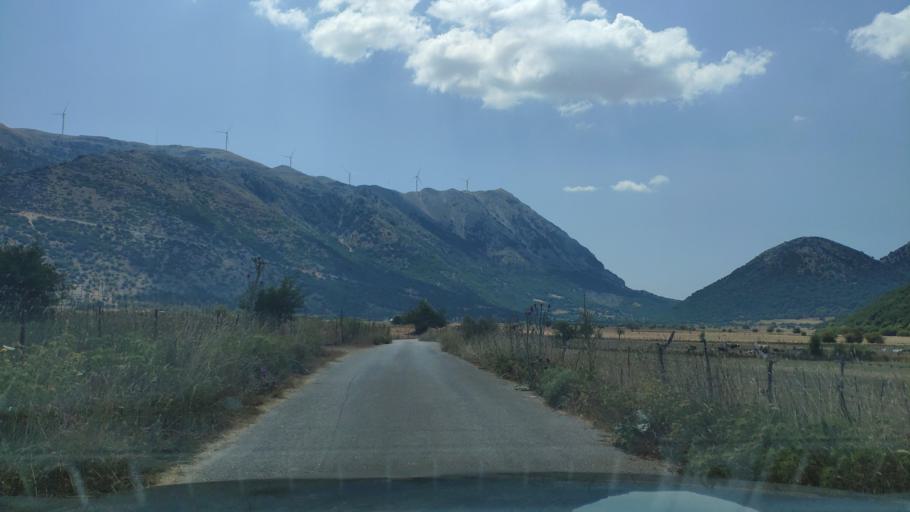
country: GR
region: West Greece
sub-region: Nomos Aitolias kai Akarnanias
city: Monastirakion
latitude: 38.7897
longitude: 20.9628
